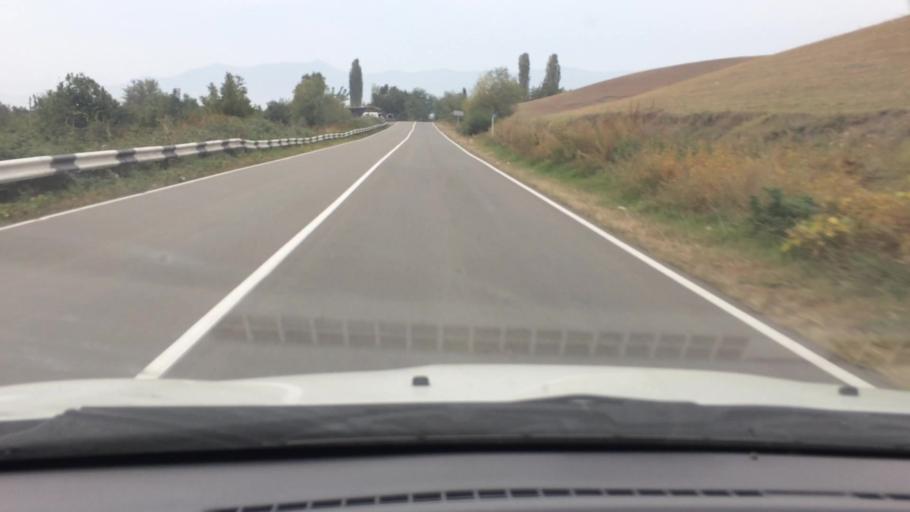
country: AM
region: Tavush
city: Bagratashen
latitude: 41.2838
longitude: 44.7906
